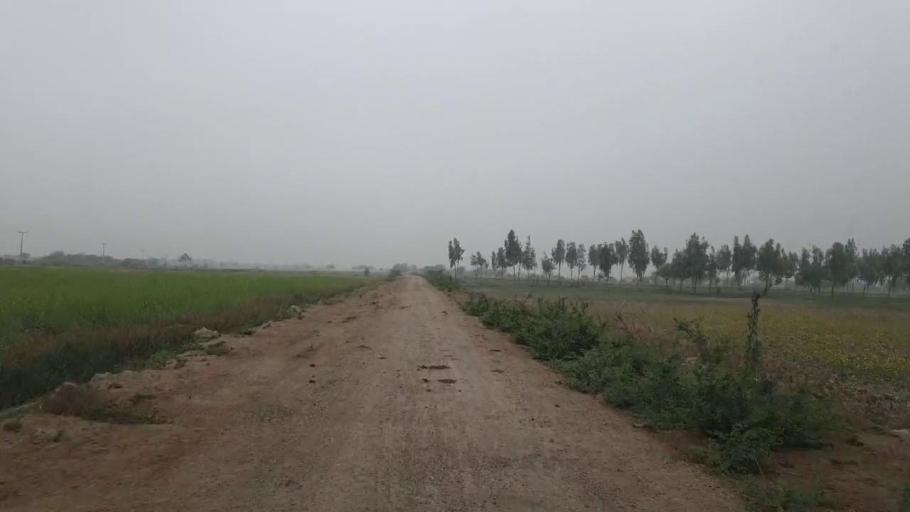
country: PK
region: Sindh
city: Badin
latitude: 24.5708
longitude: 68.6639
